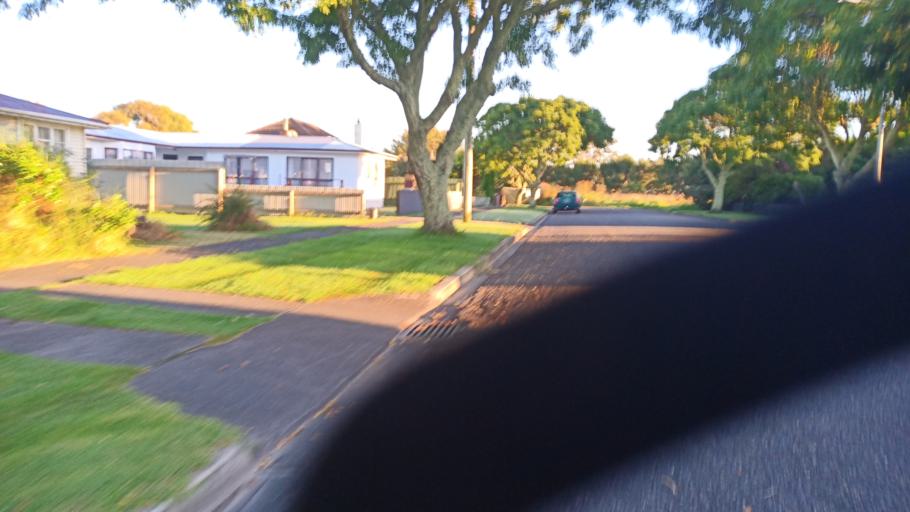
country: NZ
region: Gisborne
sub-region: Gisborne District
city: Gisborne
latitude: -38.6577
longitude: 177.9860
